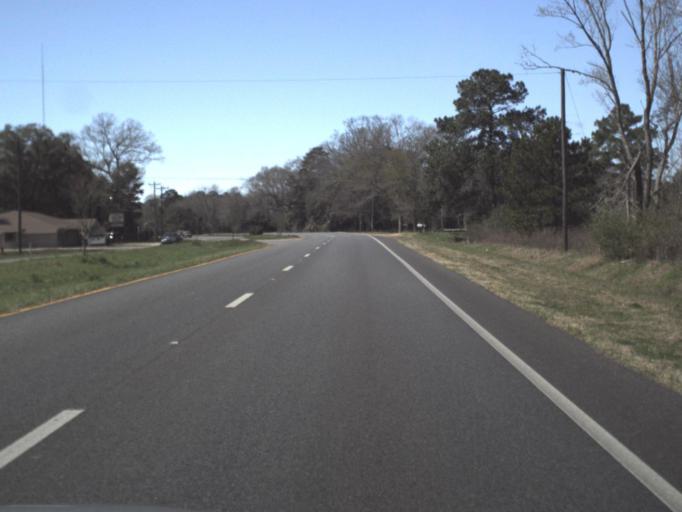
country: US
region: Florida
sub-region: Gadsden County
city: Quincy
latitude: 30.5892
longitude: -84.6246
